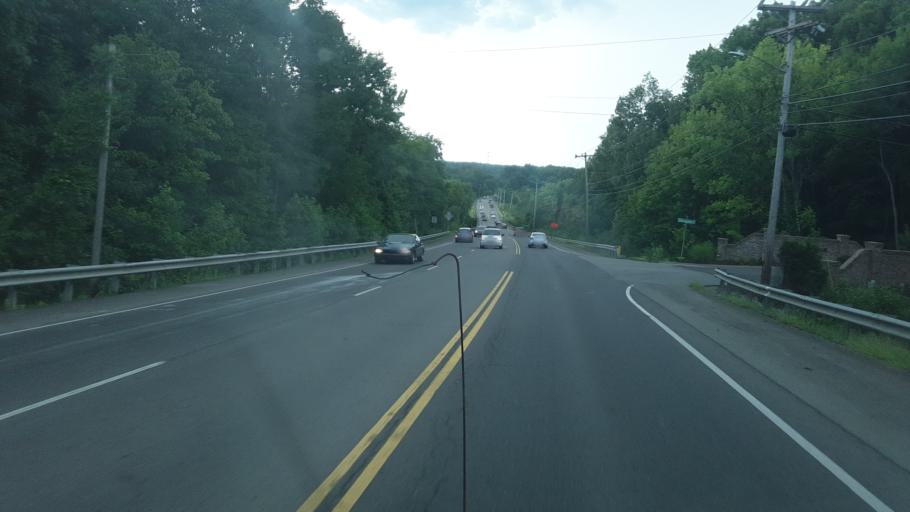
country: US
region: Tennessee
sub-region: Montgomery County
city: Clarksville
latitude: 36.5250
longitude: -87.2785
